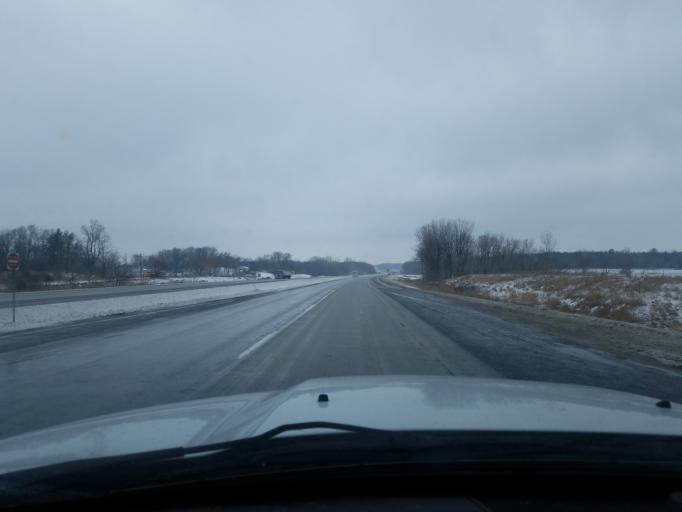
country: US
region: Indiana
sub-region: Fulton County
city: Rochester
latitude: 41.0857
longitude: -86.2409
